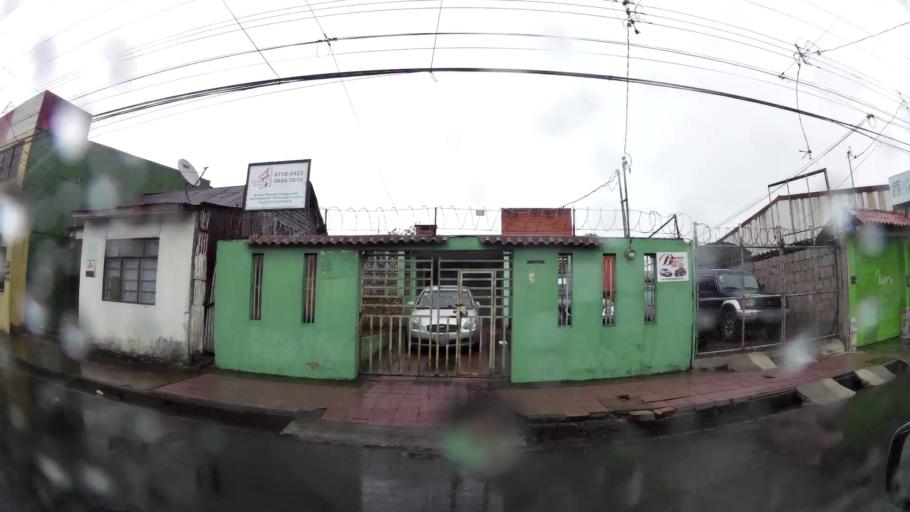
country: CR
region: Cartago
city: Cartago
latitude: 9.8642
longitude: -83.9292
